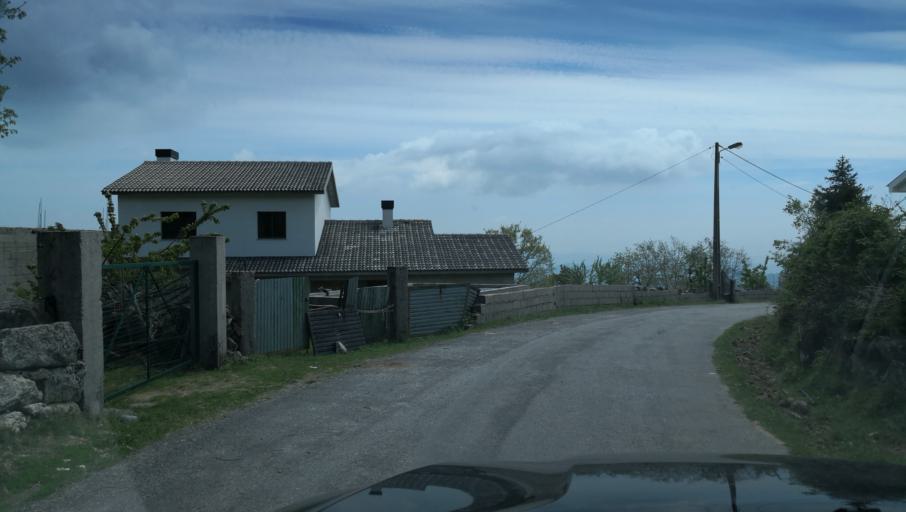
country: PT
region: Vila Real
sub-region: Vila Real
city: Vila Real
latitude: 41.2941
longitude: -7.8148
